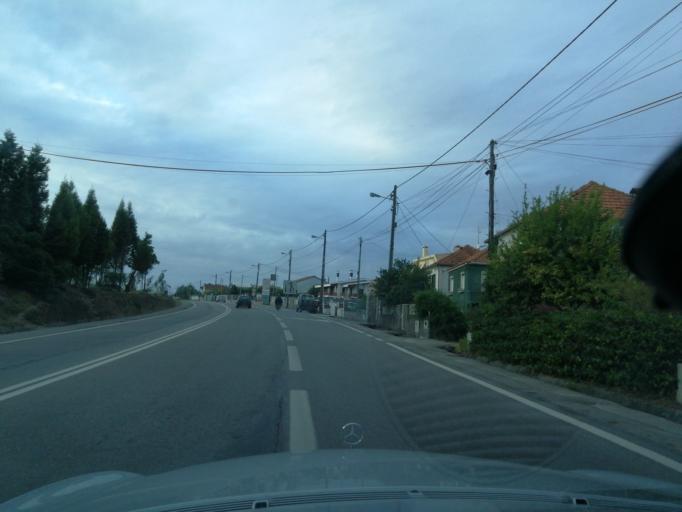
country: PT
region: Aveiro
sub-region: Agueda
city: Agueda
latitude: 40.5879
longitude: -8.4496
